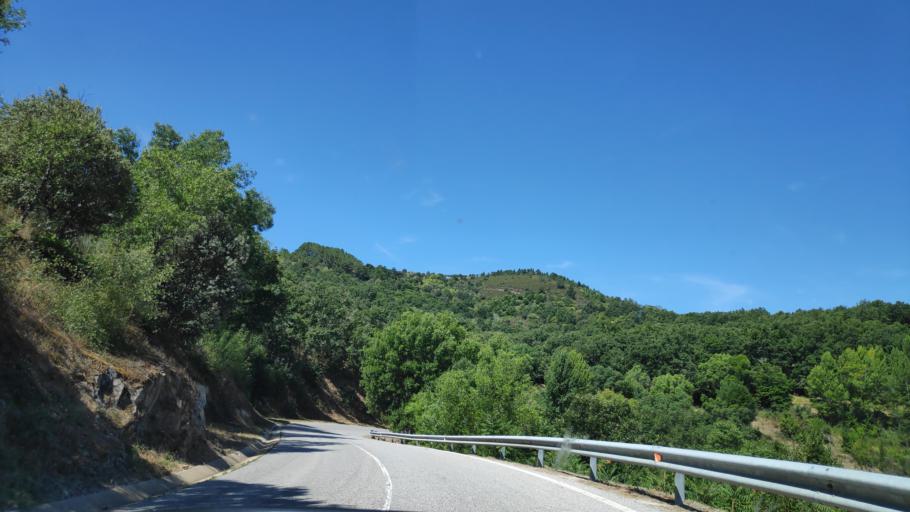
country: PT
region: Braganca
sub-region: Braganca Municipality
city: Braganca
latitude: 41.8567
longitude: -6.7469
